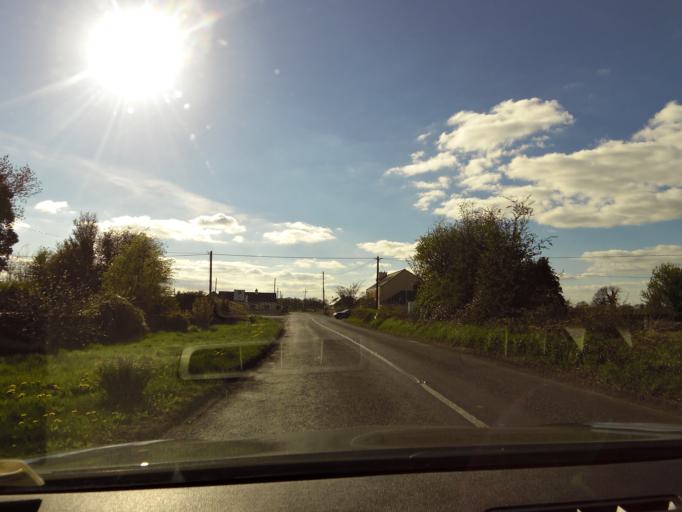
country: IE
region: Leinster
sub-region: Uibh Fhaili
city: Banagher
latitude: 53.1065
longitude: -8.0494
